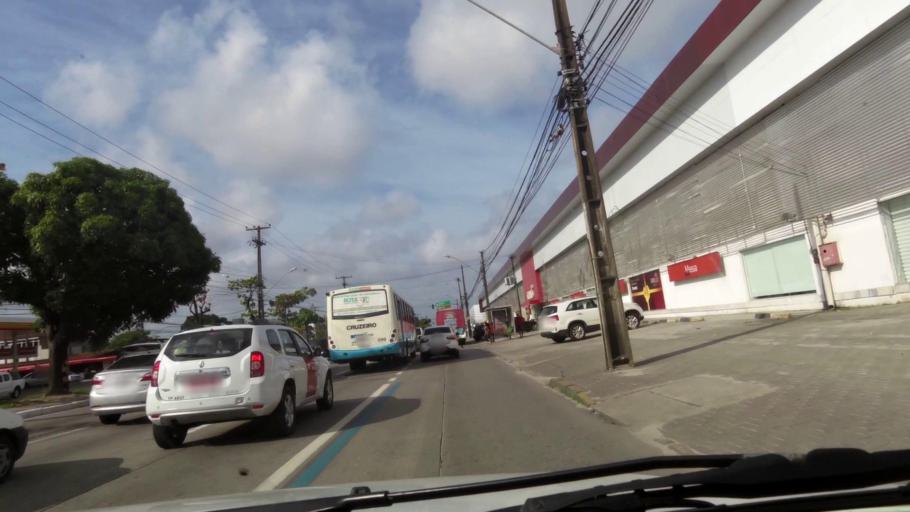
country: BR
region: Pernambuco
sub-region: Recife
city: Recife
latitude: -8.0898
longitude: -34.9081
